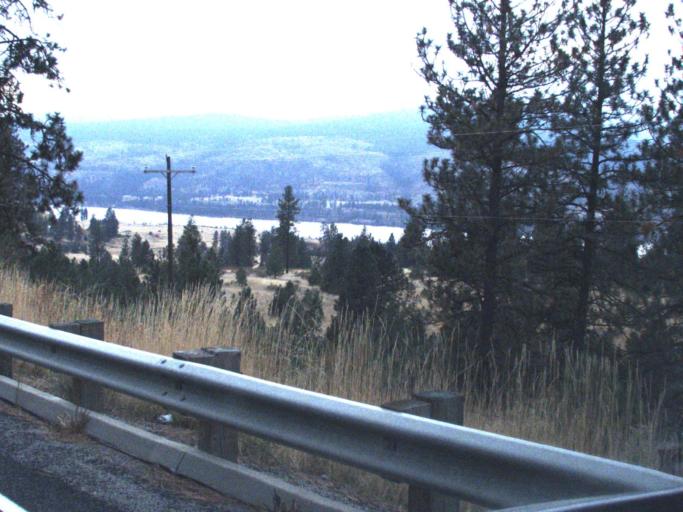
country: US
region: Washington
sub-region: Lincoln County
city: Davenport
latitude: 47.9343
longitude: -118.3193
